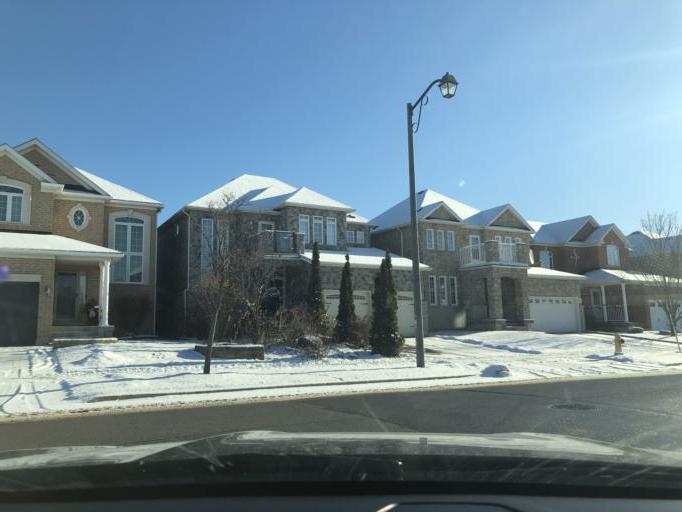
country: CA
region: Ontario
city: Scarborough
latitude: 43.7756
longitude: -79.1396
